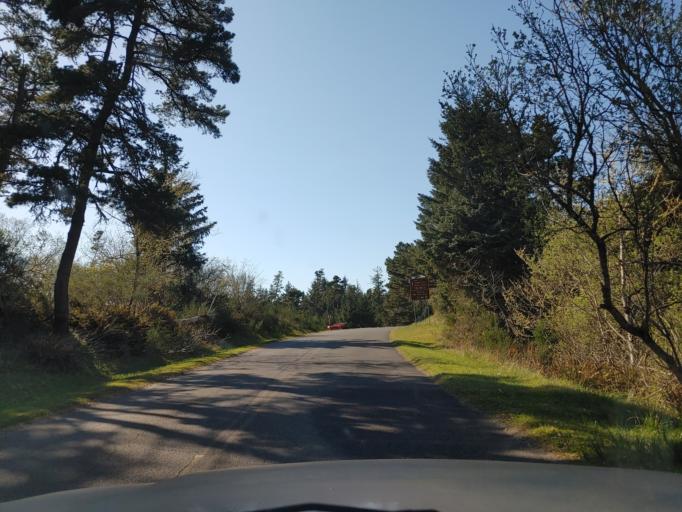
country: US
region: Oregon
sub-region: Clatsop County
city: Warrenton
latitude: 46.1796
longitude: -123.9692
